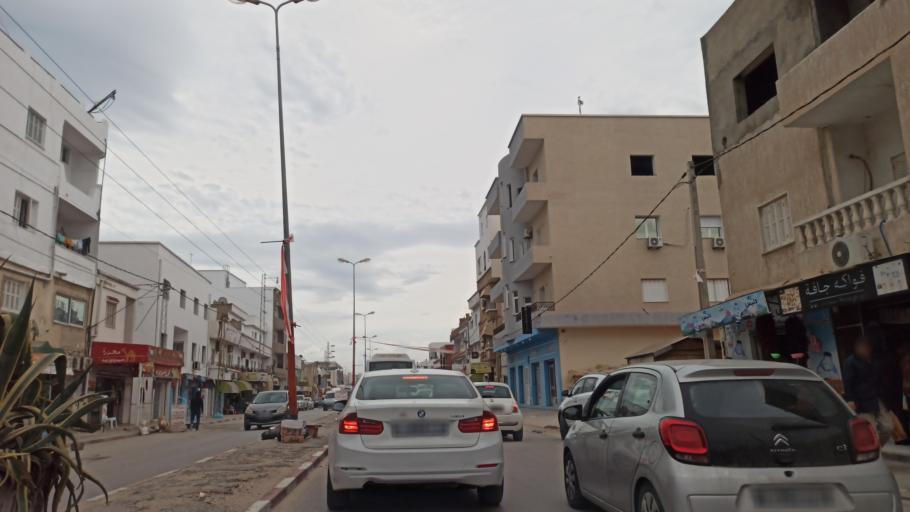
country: TN
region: Ariana
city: Ariana
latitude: 36.8668
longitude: 10.2511
